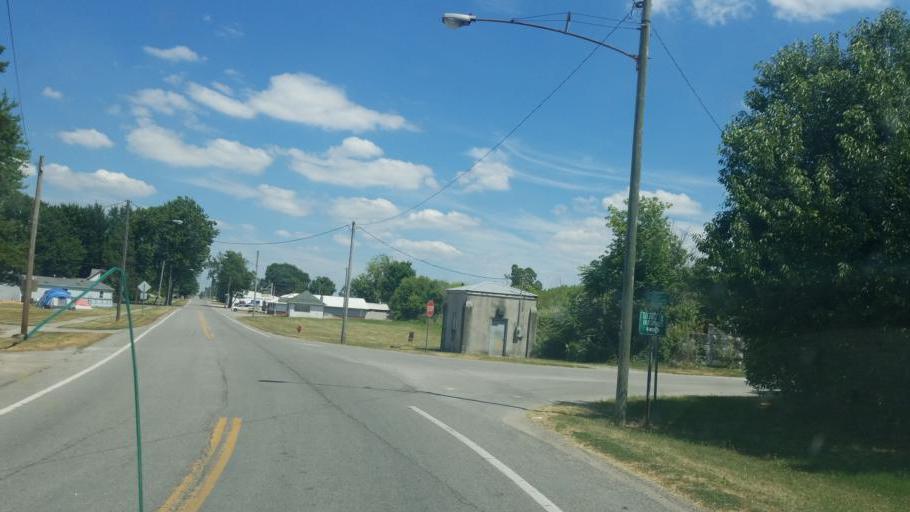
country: US
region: Ohio
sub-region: Defiance County
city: Hicksville
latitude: 41.2959
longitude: -84.7551
